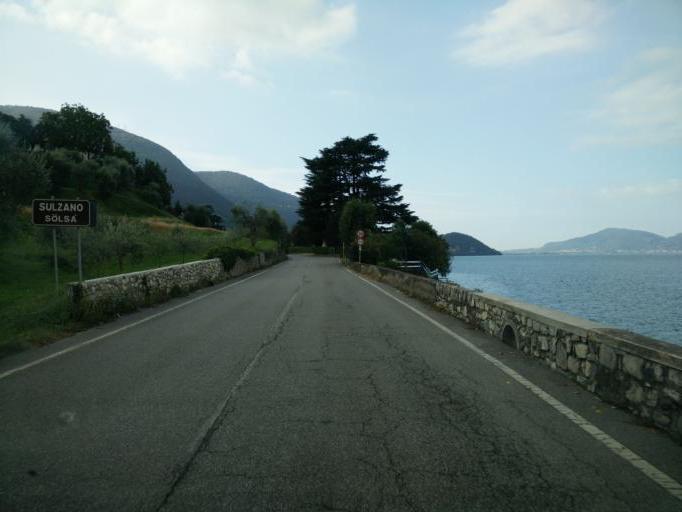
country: IT
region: Lombardy
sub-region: Provincia di Brescia
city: Sulzano
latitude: 45.6968
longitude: 10.1050
